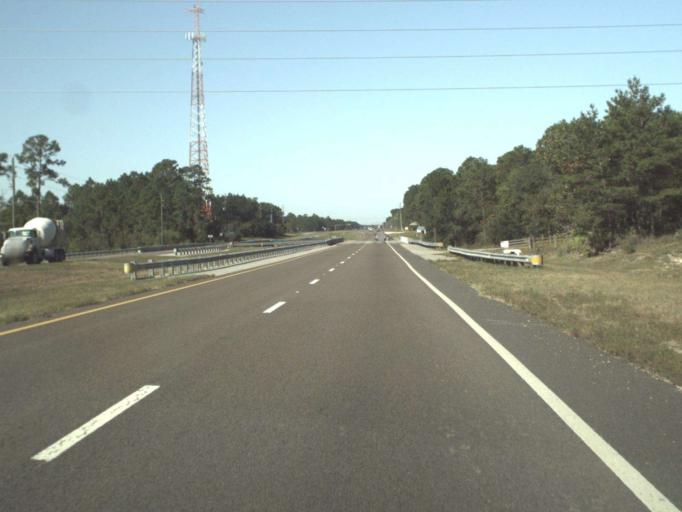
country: US
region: Florida
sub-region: Walton County
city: Seaside
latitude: 30.3568
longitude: -86.1048
